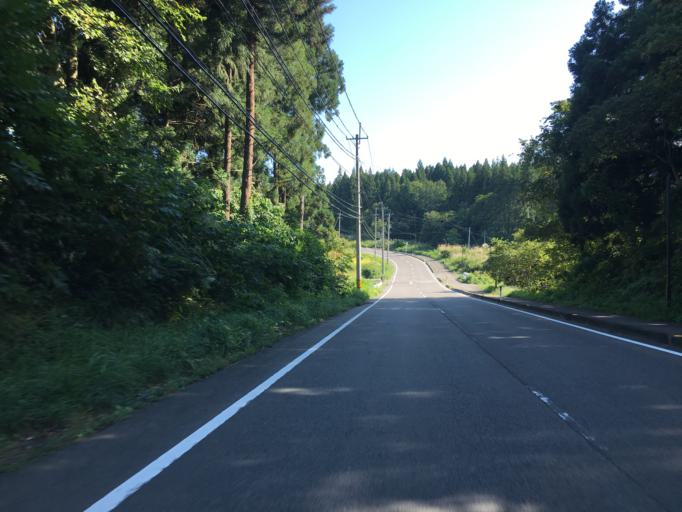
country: JP
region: Fukushima
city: Kitakata
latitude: 37.5955
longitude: 139.6537
